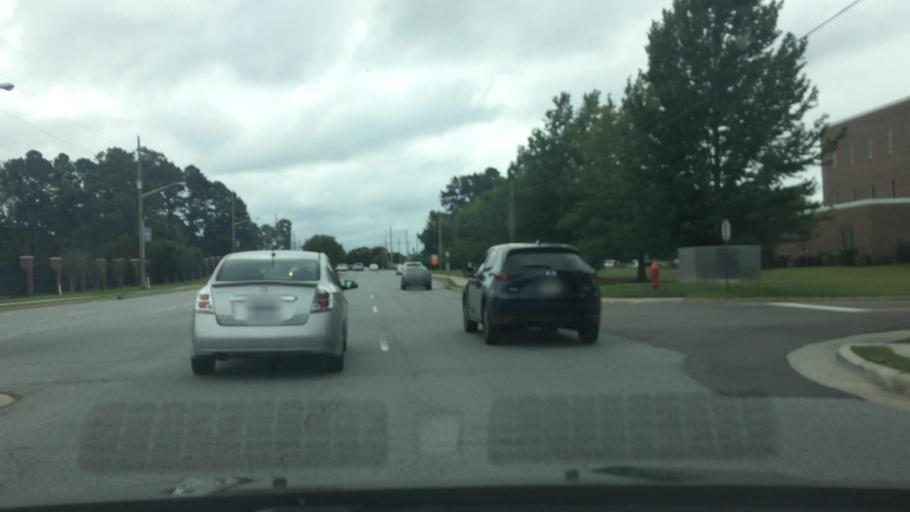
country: US
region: North Carolina
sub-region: Pitt County
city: Greenville
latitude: 35.5917
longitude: -77.3684
